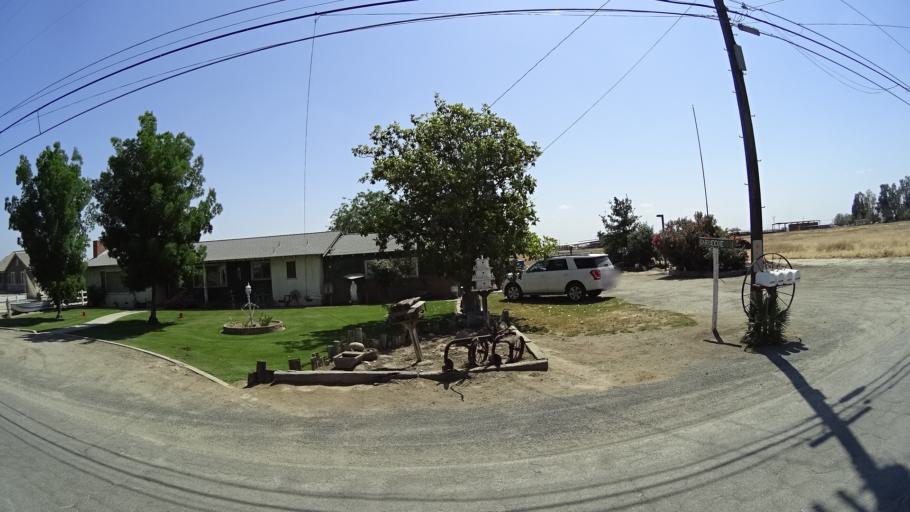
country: US
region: California
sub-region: Kings County
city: Home Garden
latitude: 36.3209
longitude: -119.6213
